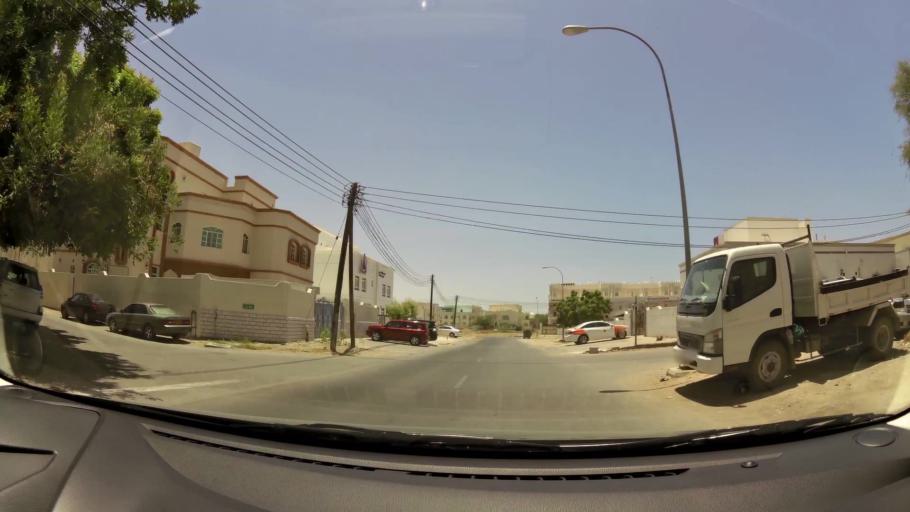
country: OM
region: Muhafazat Masqat
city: Bawshar
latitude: 23.6005
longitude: 58.3861
